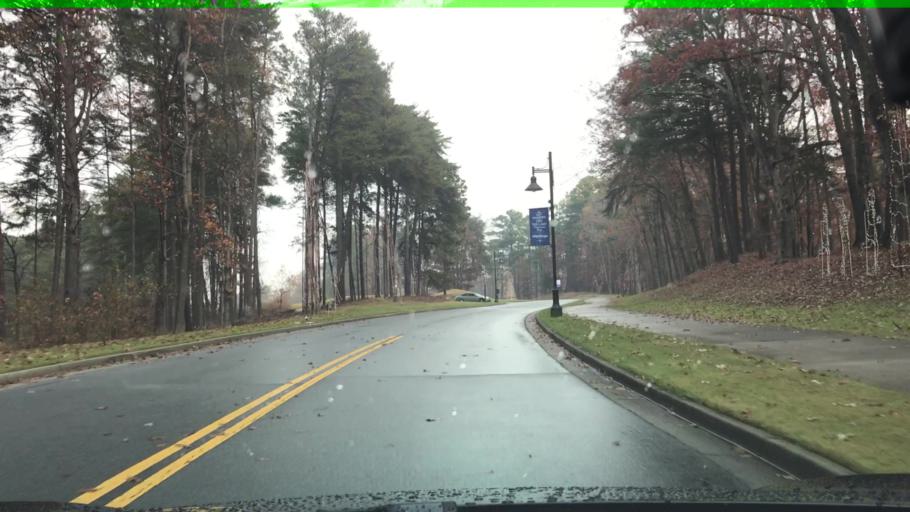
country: US
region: Georgia
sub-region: Gwinnett County
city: Buford
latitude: 34.1764
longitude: -84.0252
